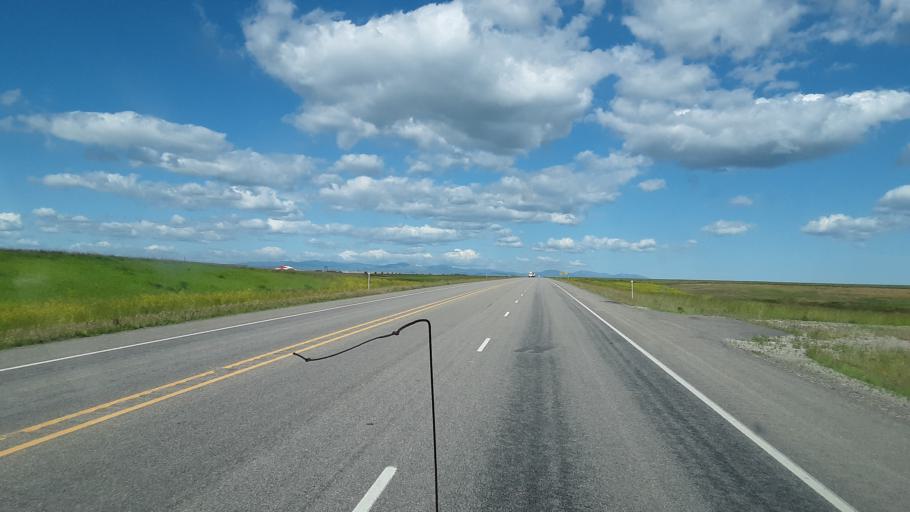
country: US
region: Montana
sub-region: Fergus County
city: Lewistown
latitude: 46.9984
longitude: -109.8111
